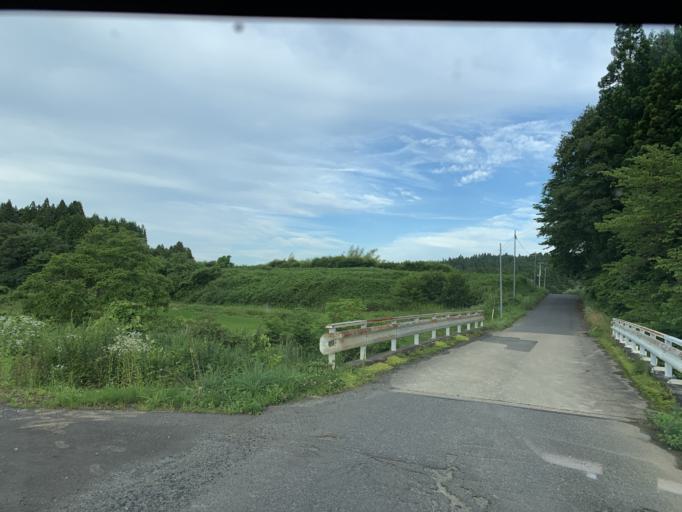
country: JP
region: Iwate
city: Ichinoseki
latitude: 38.9122
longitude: 141.0238
